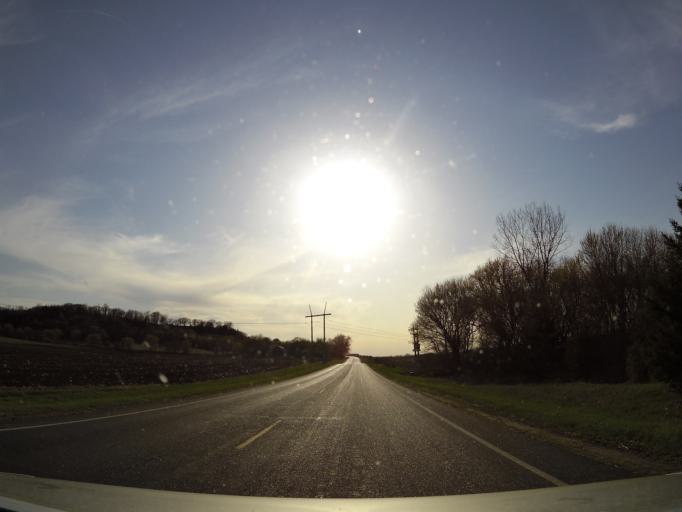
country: US
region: Wisconsin
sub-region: Pierce County
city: River Falls
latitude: 44.8336
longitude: -92.6486
